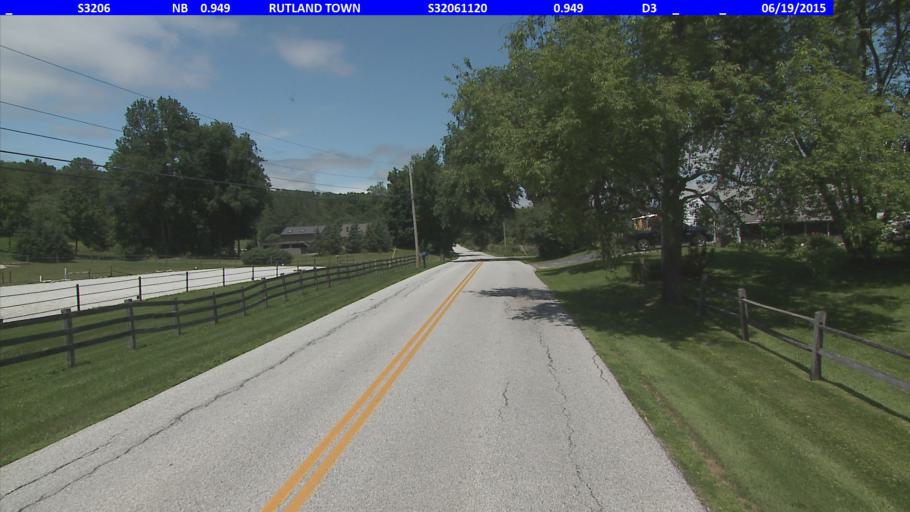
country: US
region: Vermont
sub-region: Rutland County
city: Rutland
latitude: 43.6428
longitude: -72.9932
